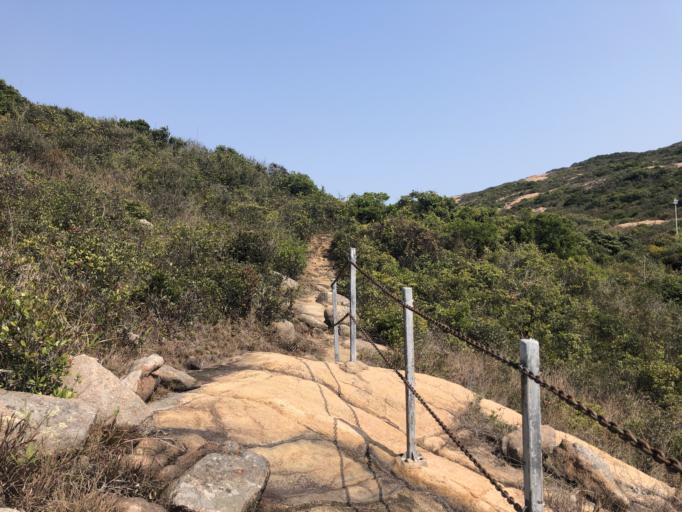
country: HK
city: Sok Kwu Wan
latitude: 22.1691
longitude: 114.2553
